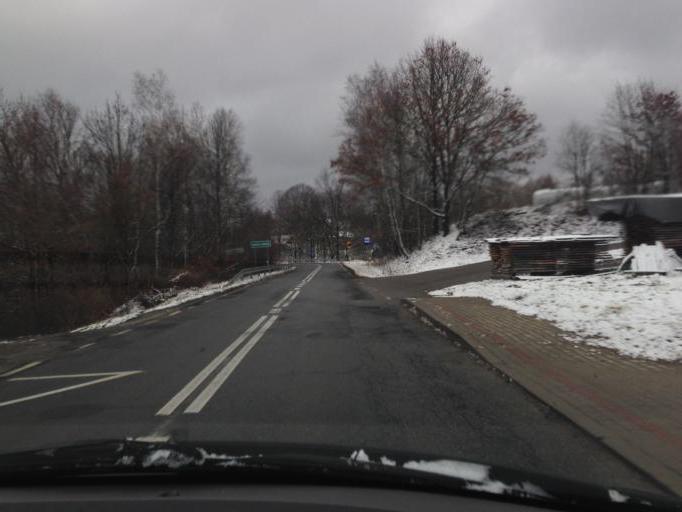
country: PL
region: Lesser Poland Voivodeship
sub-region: Powiat brzeski
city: Iwkowa
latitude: 49.8573
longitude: 20.5649
